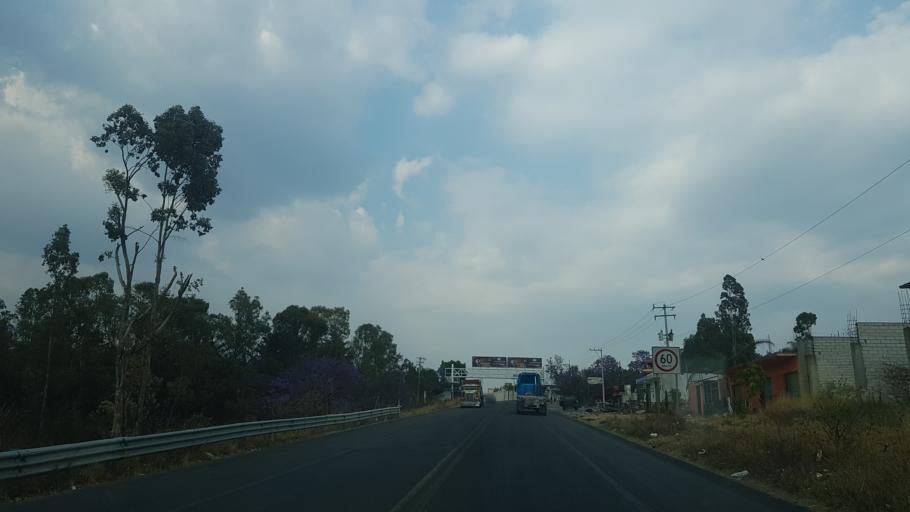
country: MX
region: Puebla
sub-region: Santa Isabel Cholula
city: Santa Ana Acozautla
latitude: 18.9555
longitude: -98.3882
